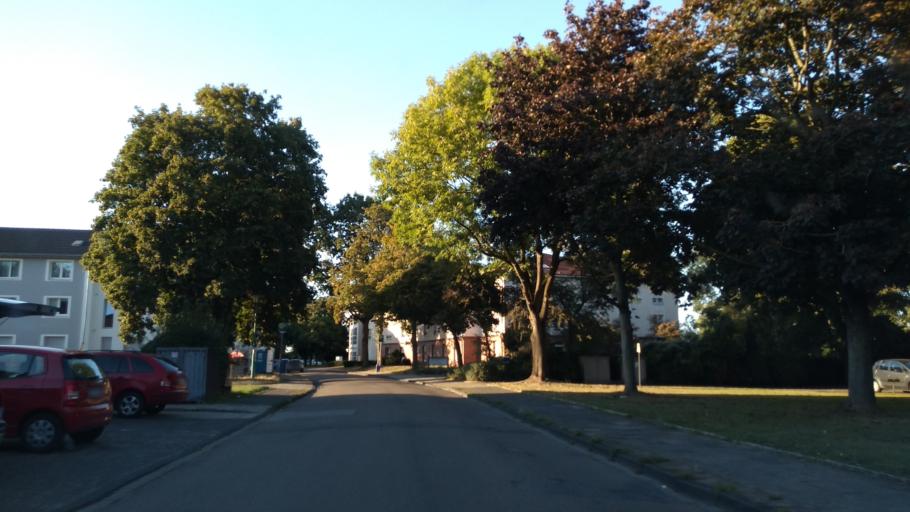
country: DE
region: North Rhine-Westphalia
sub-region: Regierungsbezirk Dusseldorf
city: Dinslaken
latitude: 51.5500
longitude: 6.7179
